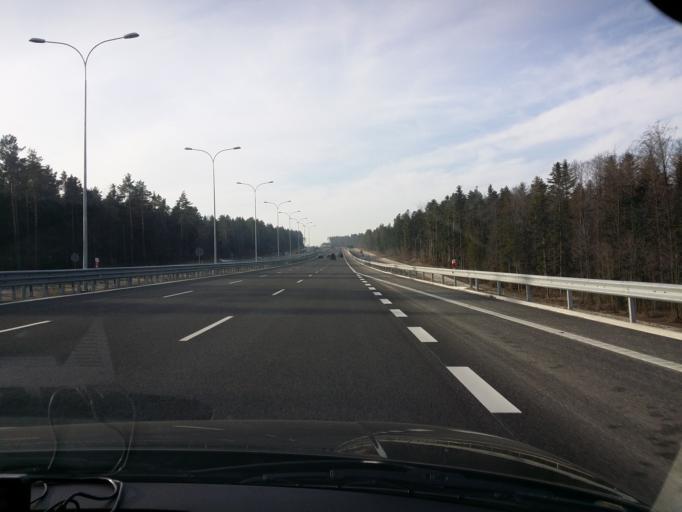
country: PL
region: Swietokrzyskie
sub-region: Powiat skarzyski
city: Skarzysko-Kamienna
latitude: 51.1550
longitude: 20.8484
